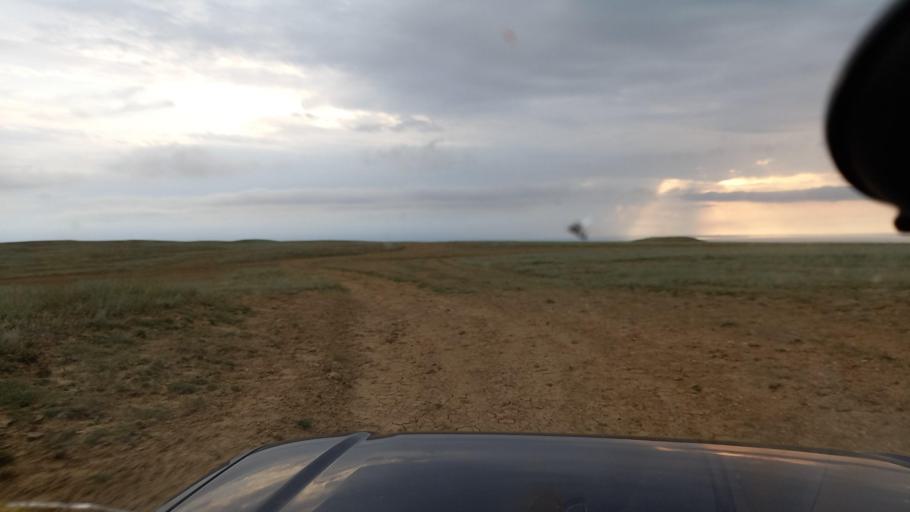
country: RU
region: Krasnodarskiy
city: Taman'
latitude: 45.2069
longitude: 36.7879
